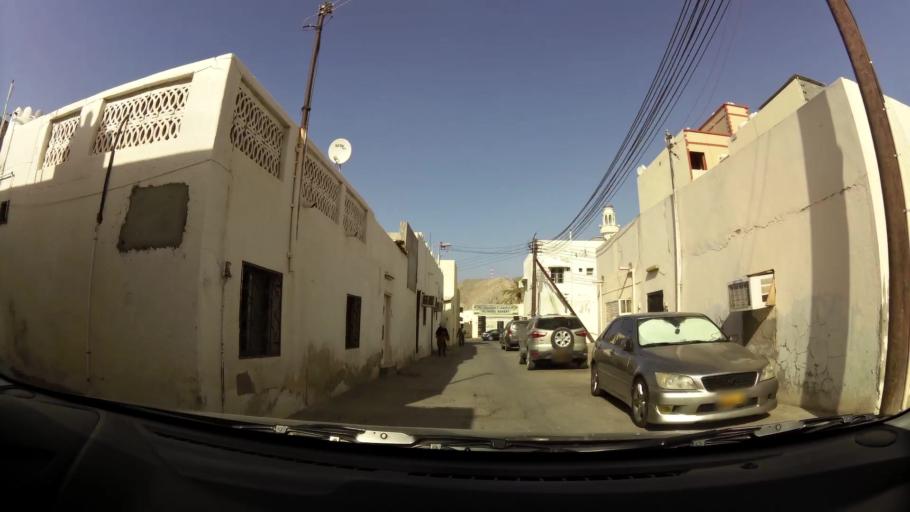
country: OM
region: Muhafazat Masqat
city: Muscat
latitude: 23.5848
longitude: 58.5176
